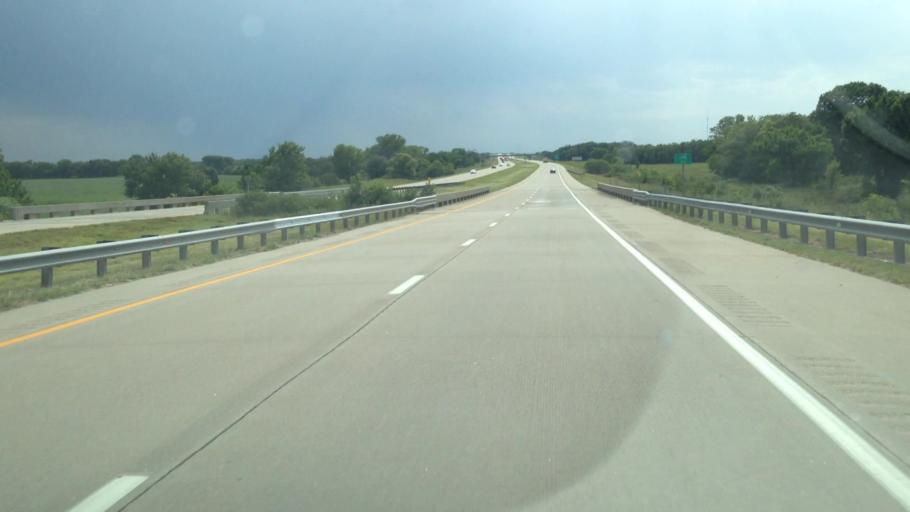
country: US
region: Kansas
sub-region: Osage County
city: Lyndon
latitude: 38.4378
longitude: -95.6953
